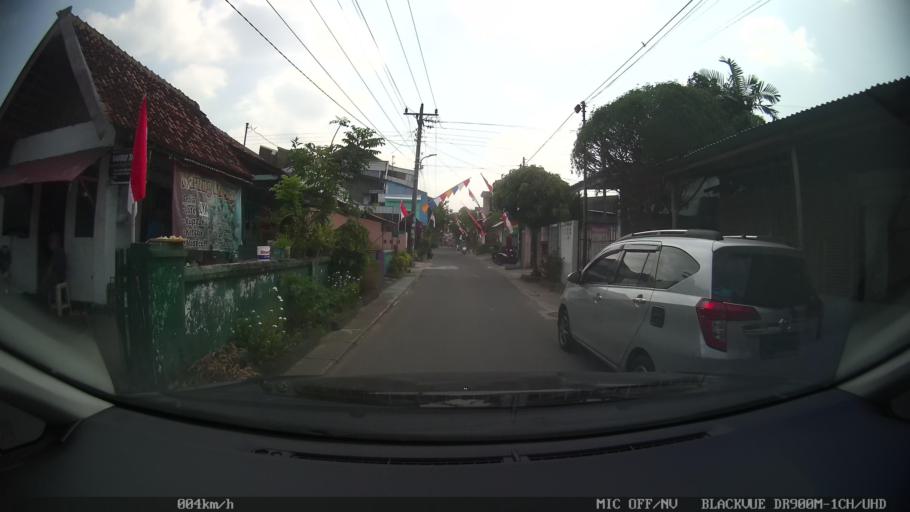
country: ID
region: Daerah Istimewa Yogyakarta
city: Yogyakarta
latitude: -7.8075
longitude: 110.3824
